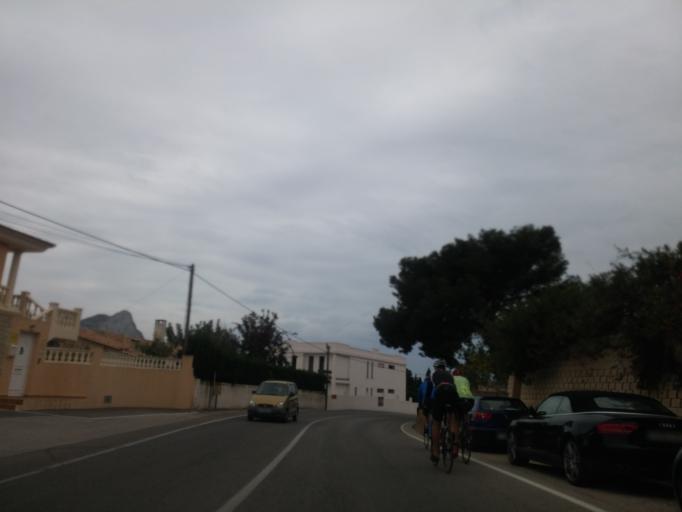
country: ES
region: Valencia
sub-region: Provincia de Alicante
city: Calp
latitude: 38.6585
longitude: 0.0787
